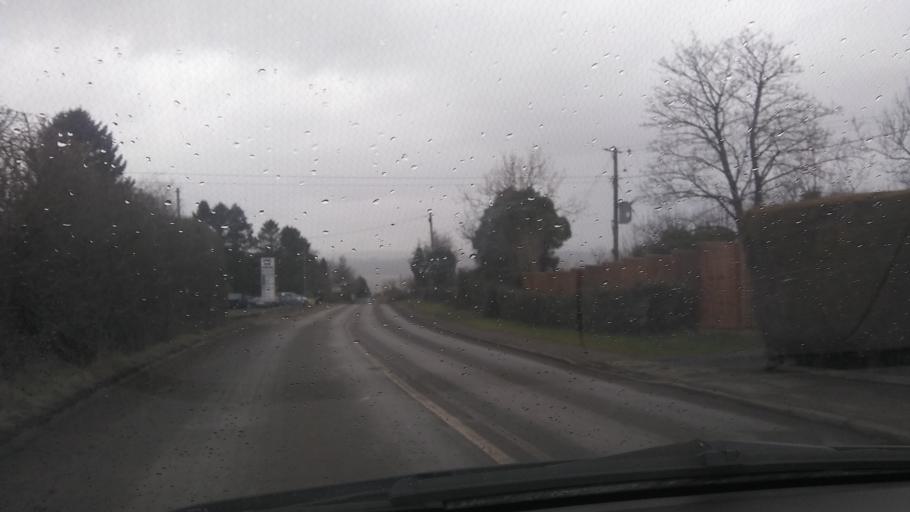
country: GB
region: England
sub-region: Worcestershire
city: Tenbury Wells
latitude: 52.3783
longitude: -2.6173
